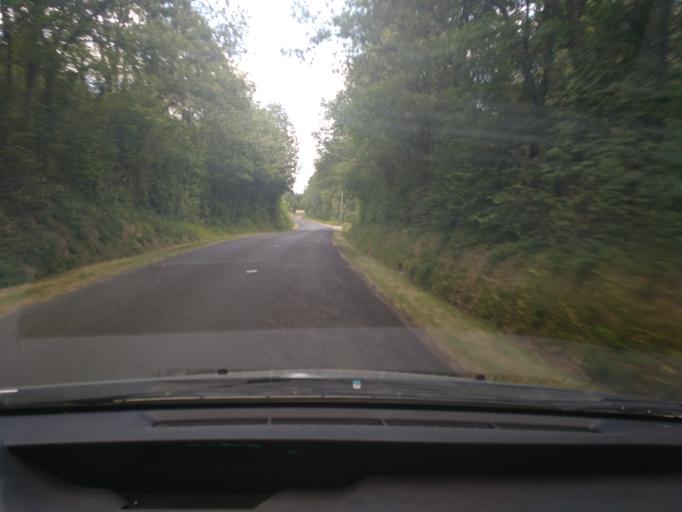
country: FR
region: Pays de la Loire
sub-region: Departement de Maine-et-Loire
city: Bauge-en-Anjou
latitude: 47.5492
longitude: -0.0643
